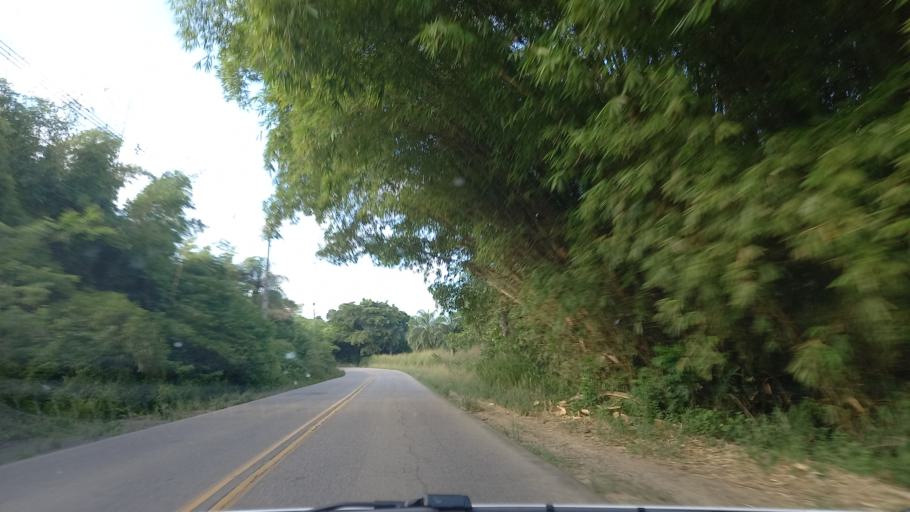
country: BR
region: Pernambuco
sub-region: Rio Formoso
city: Rio Formoso
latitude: -8.6426
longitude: -35.1190
